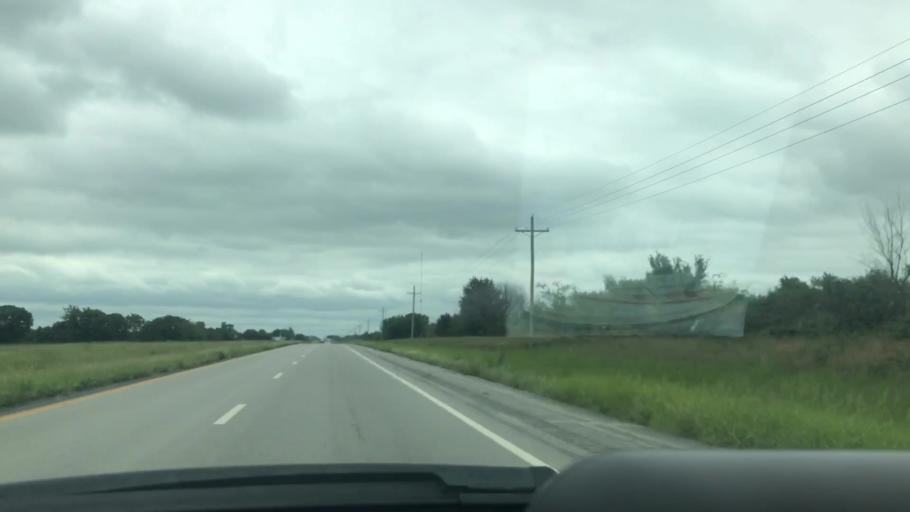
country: US
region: Oklahoma
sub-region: Mayes County
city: Pryor
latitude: 36.4137
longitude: -95.2801
